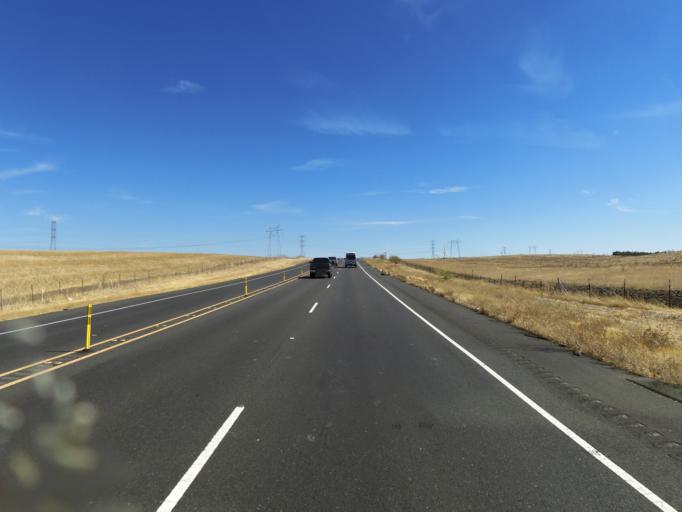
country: US
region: California
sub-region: Contra Costa County
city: Pittsburg
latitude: 38.1903
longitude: -121.8564
